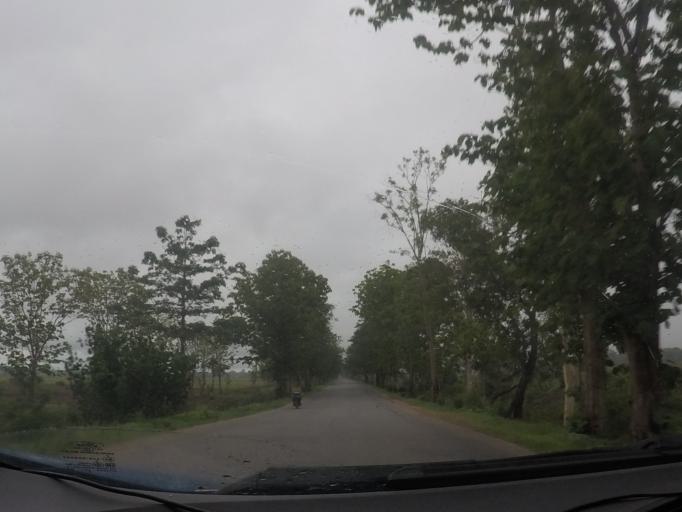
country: MM
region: Bago
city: Paungde
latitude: 18.1674
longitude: 95.6627
